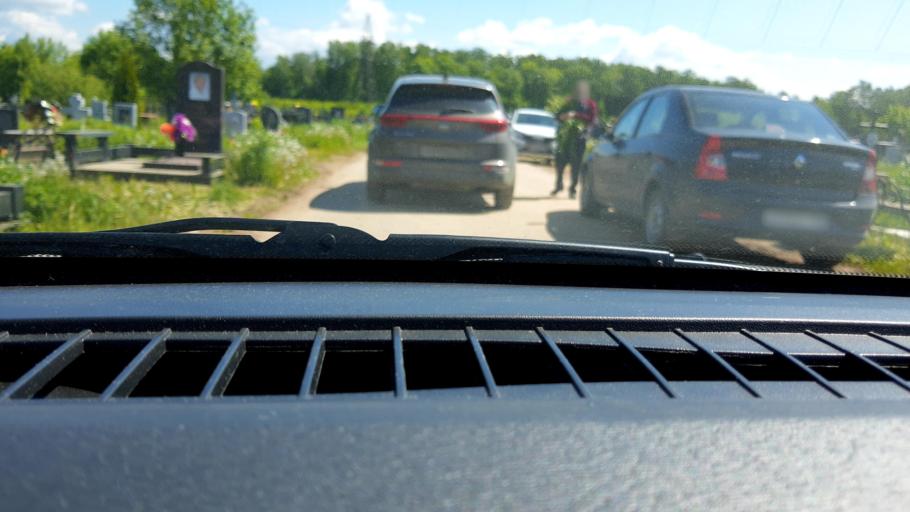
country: RU
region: Nizjnij Novgorod
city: Afonino
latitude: 56.2312
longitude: 44.0801
